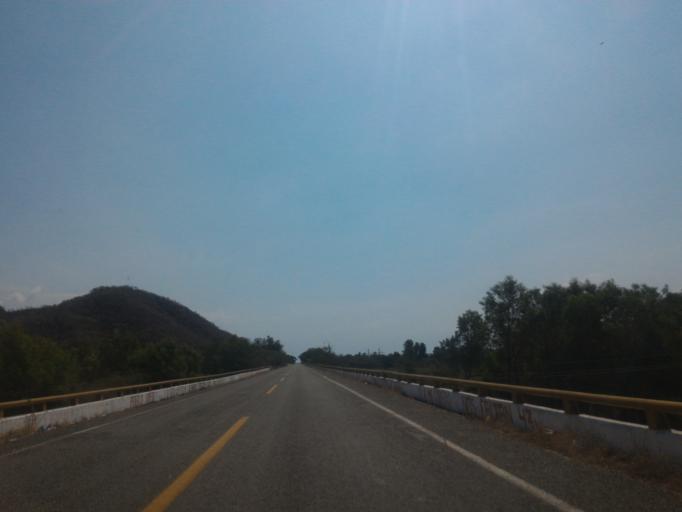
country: MX
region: Michoacan
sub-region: Coalcoman de Vazquez Pallares
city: Coalcoman de Vazquez Pallares
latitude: 18.2788
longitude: -103.3534
